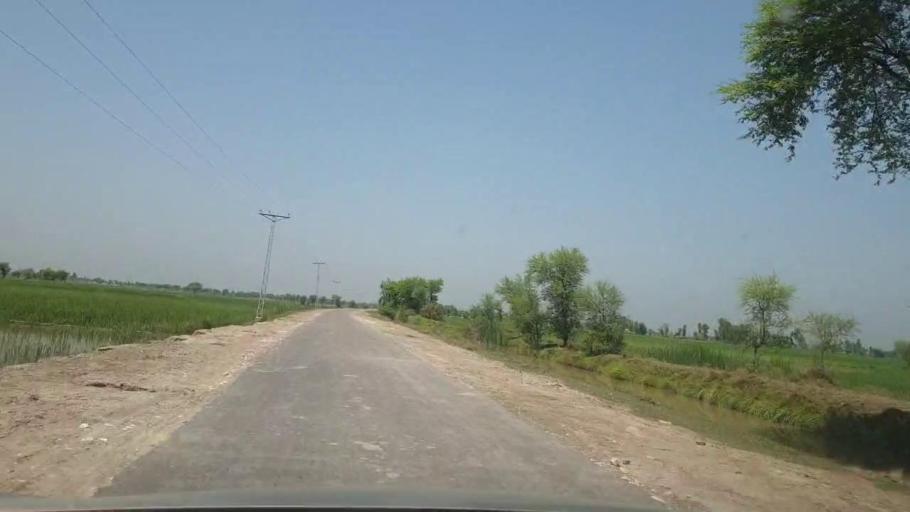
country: PK
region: Sindh
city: Warah
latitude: 27.4726
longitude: 67.7622
